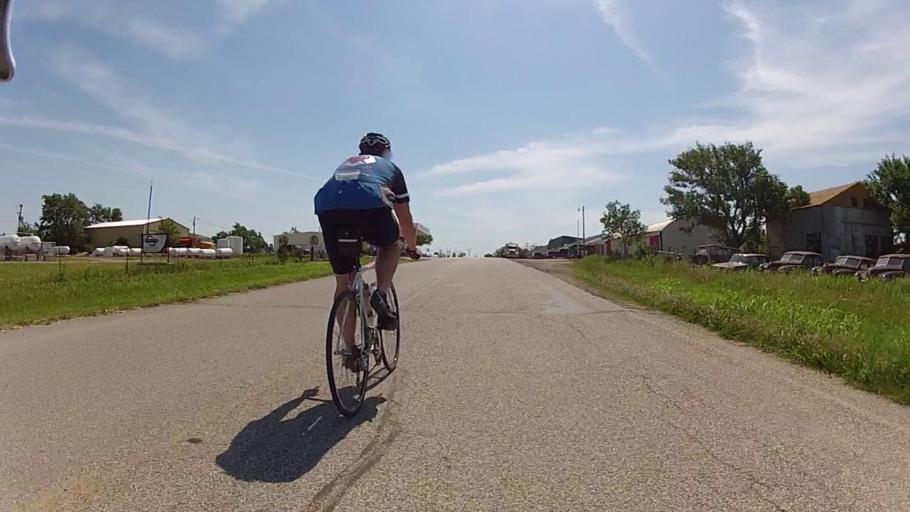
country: US
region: Kansas
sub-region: Chautauqua County
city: Sedan
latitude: 37.1104
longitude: -96.5093
